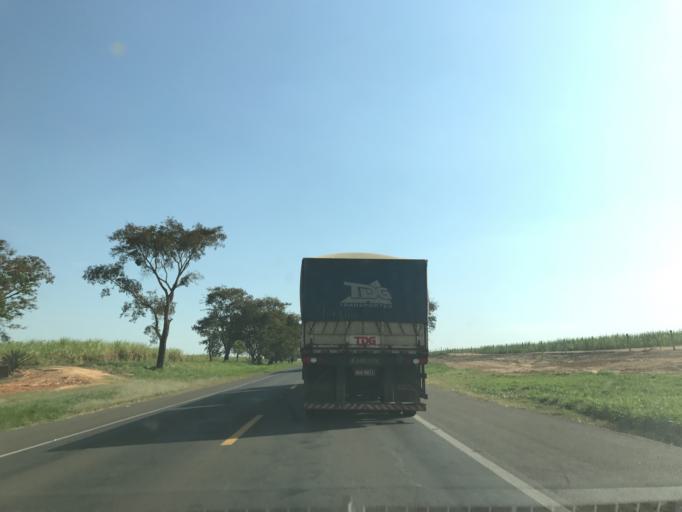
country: BR
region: Sao Paulo
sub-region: Penapolis
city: Penapolis
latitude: -21.4701
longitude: -50.1877
